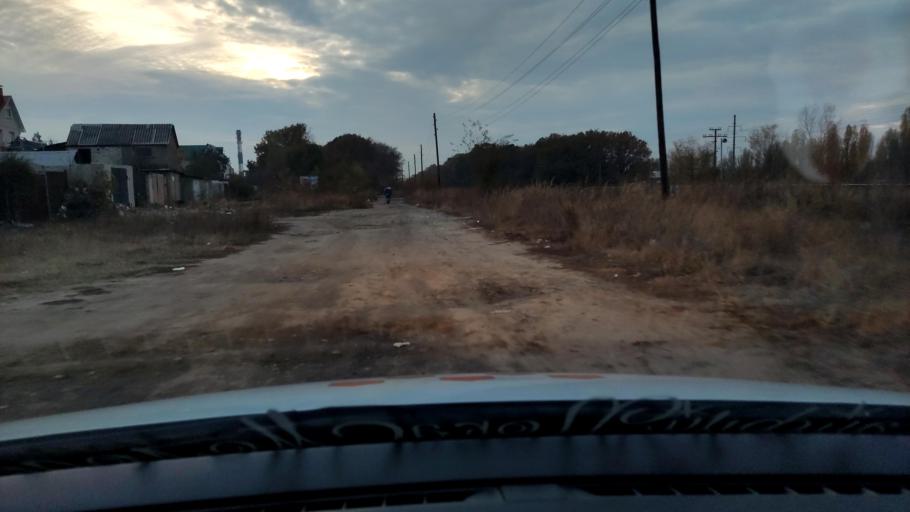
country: RU
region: Voronezj
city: Pridonskoy
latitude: 51.6634
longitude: 39.1221
